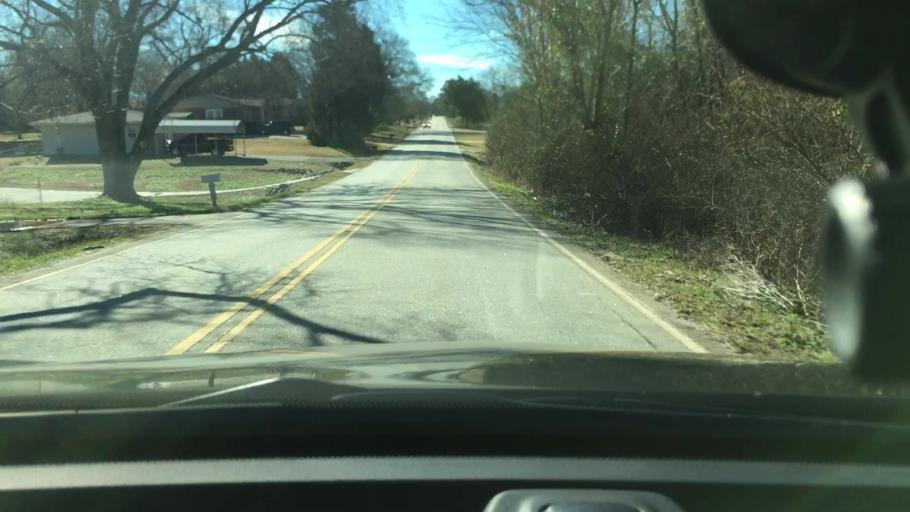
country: US
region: South Carolina
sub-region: Spartanburg County
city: Pacolet
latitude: 34.9102
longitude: -81.7711
